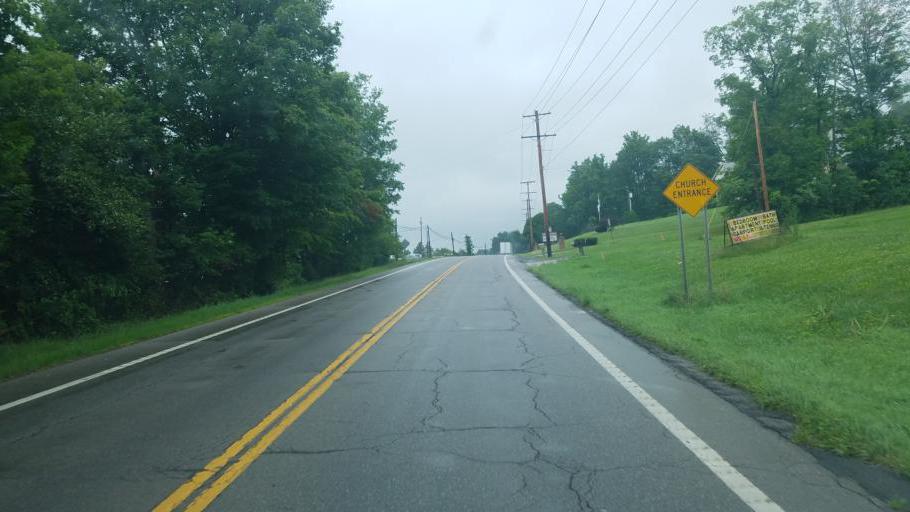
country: US
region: Ohio
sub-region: Richland County
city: Lexington
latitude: 40.6879
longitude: -82.5650
